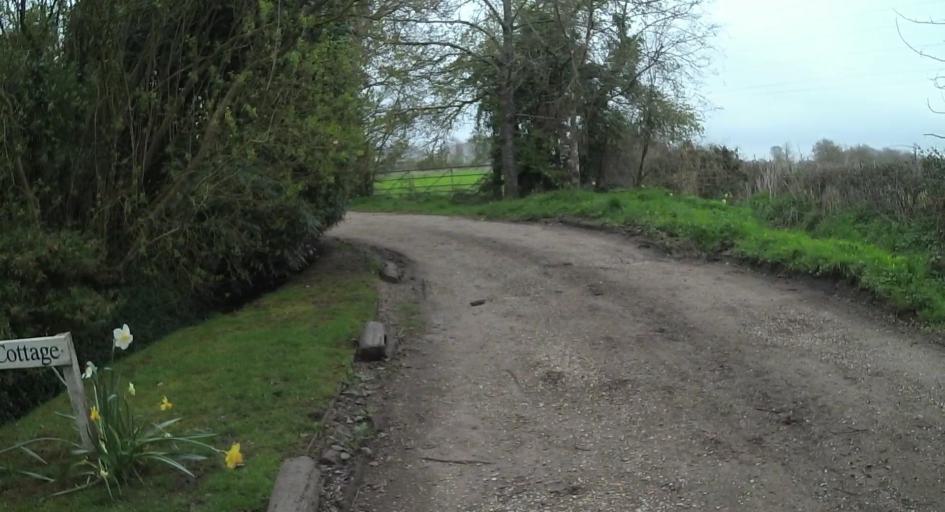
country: GB
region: England
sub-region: West Berkshire
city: Arborfield
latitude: 51.4065
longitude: -0.9096
